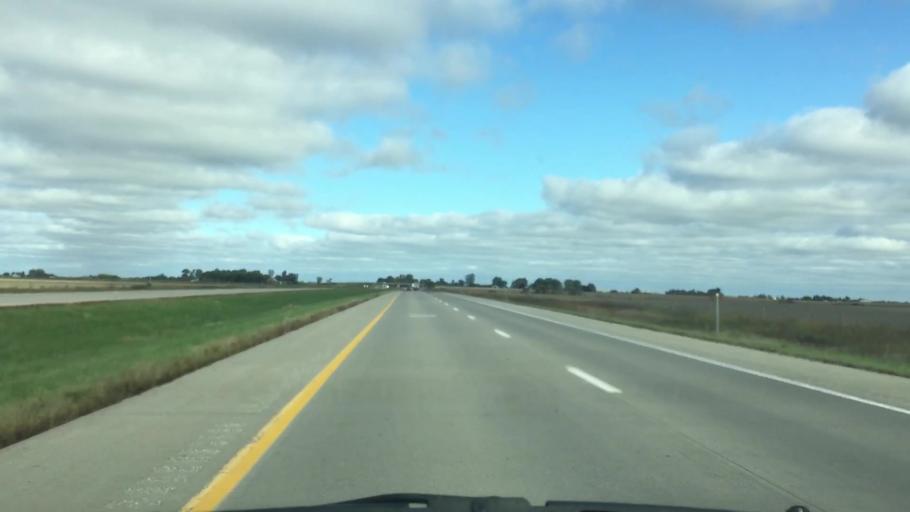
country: US
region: Iowa
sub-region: Clarke County
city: Osceola
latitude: 40.9311
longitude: -93.7975
